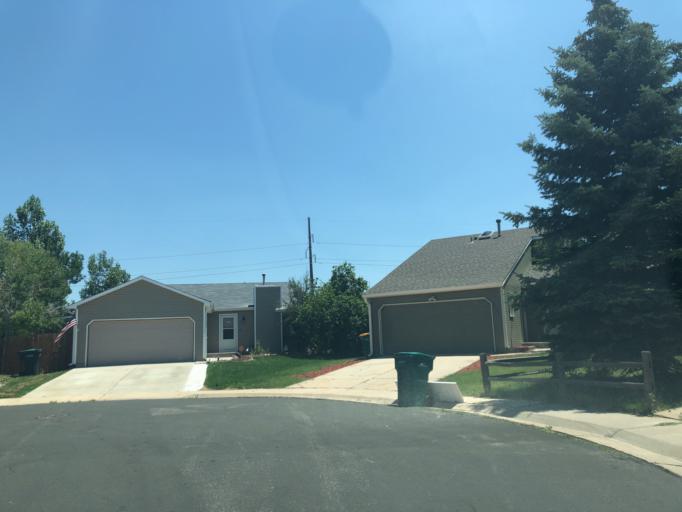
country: US
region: Colorado
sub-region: Arapahoe County
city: Dove Valley
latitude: 39.6279
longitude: -104.7553
